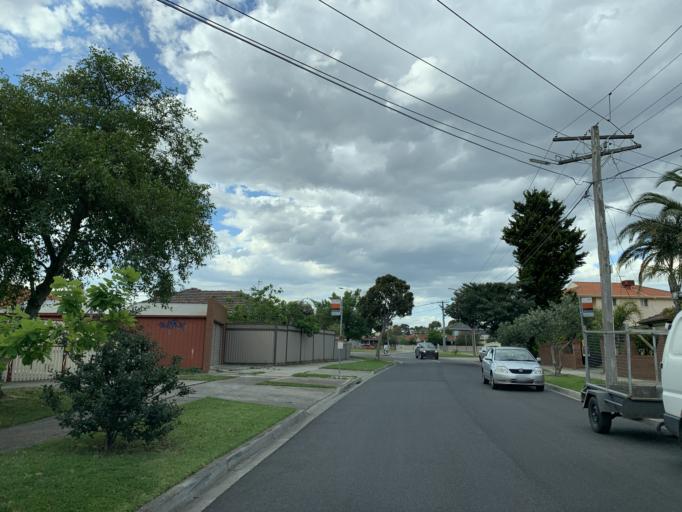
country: AU
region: Victoria
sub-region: Moonee Valley
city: Keilor East
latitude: -37.7513
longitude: 144.8556
